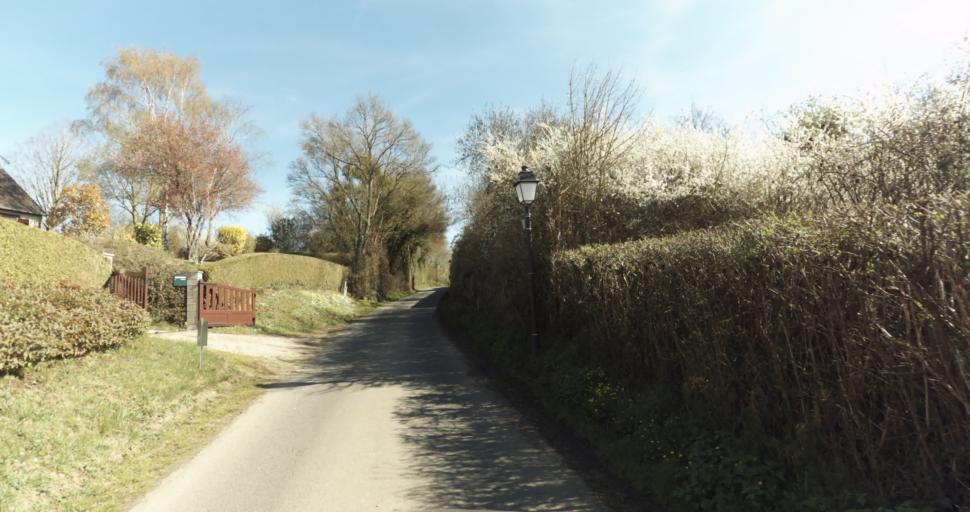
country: FR
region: Lower Normandy
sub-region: Departement du Calvados
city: Saint-Pierre-sur-Dives
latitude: 49.0515
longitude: -0.0215
